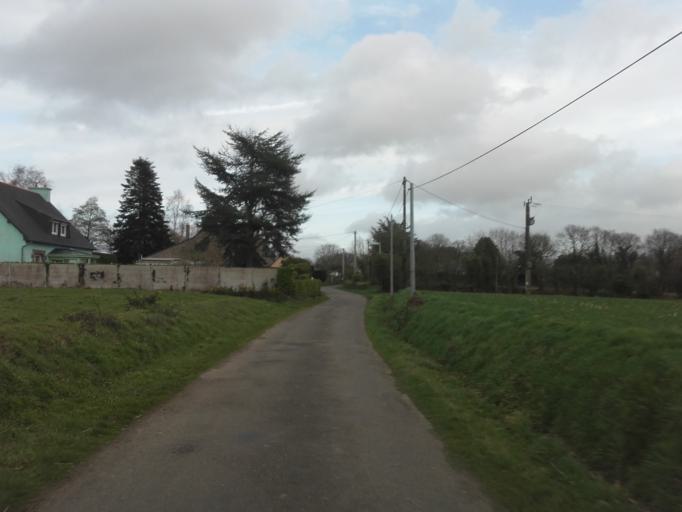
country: FR
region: Brittany
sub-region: Departement des Cotes-d'Armor
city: Lanvollon
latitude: 48.6505
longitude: -2.9799
